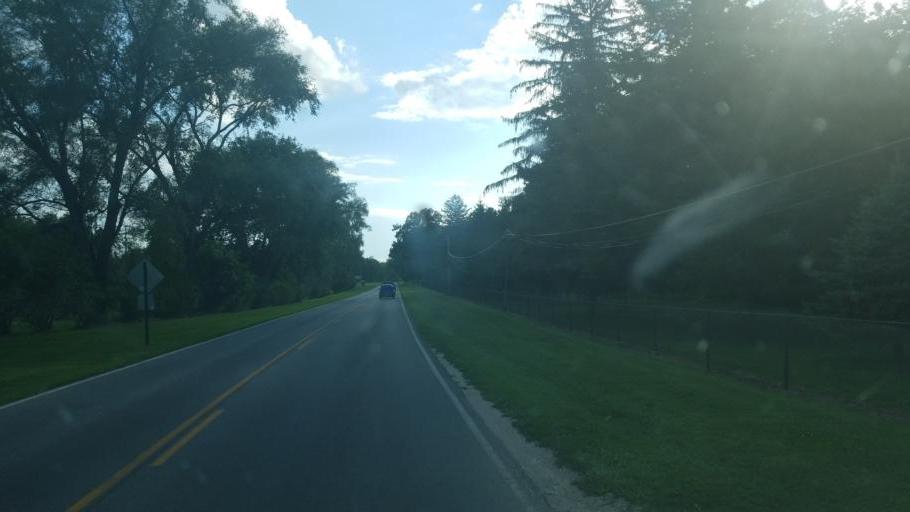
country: US
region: Ohio
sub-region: Sandusky County
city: Ballville
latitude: 41.3313
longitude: -83.1234
